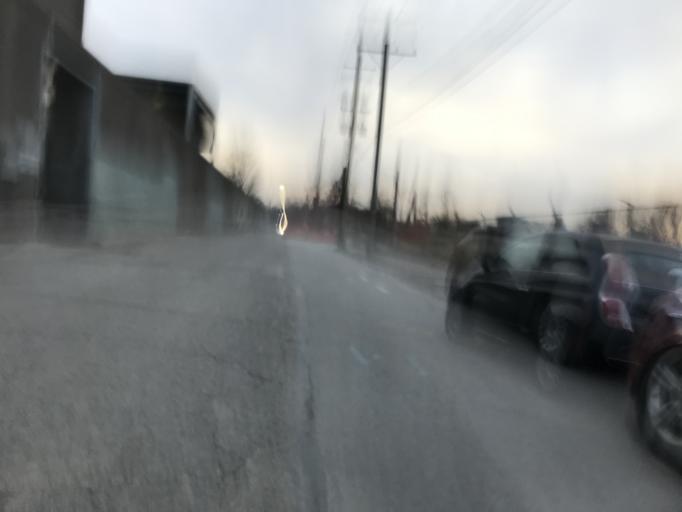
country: US
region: Indiana
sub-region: Clark County
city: Jeffersonville
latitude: 38.2573
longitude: -85.7307
